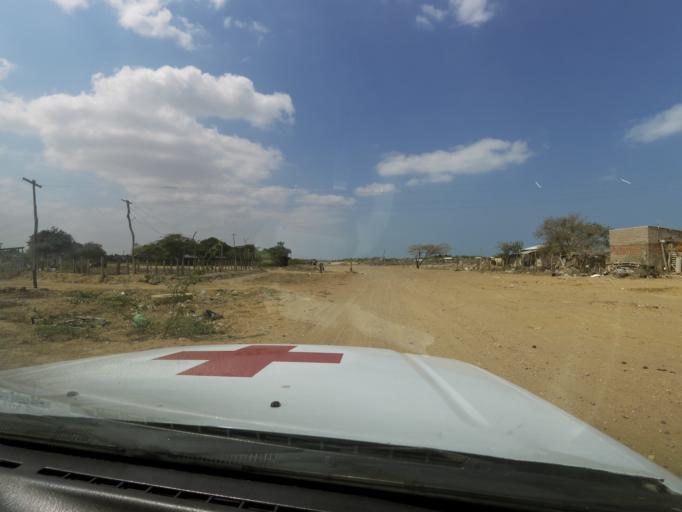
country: CO
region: La Guajira
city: Riohacha
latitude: 11.5221
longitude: -72.9179
